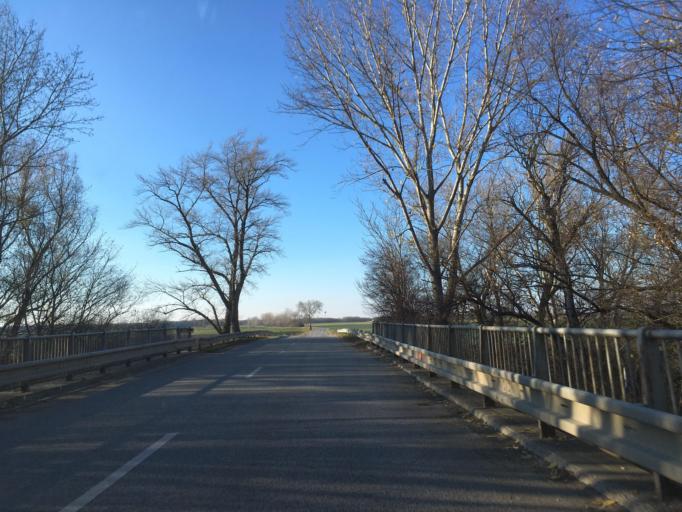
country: SK
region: Nitriansky
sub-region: Okres Komarno
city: Hurbanovo
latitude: 47.8944
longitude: 18.1866
